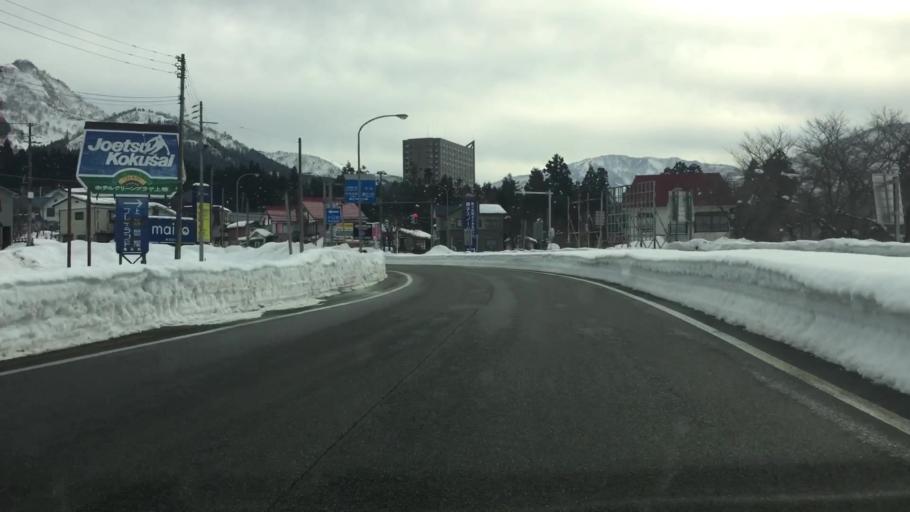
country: JP
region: Niigata
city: Shiozawa
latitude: 36.9928
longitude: 138.8213
